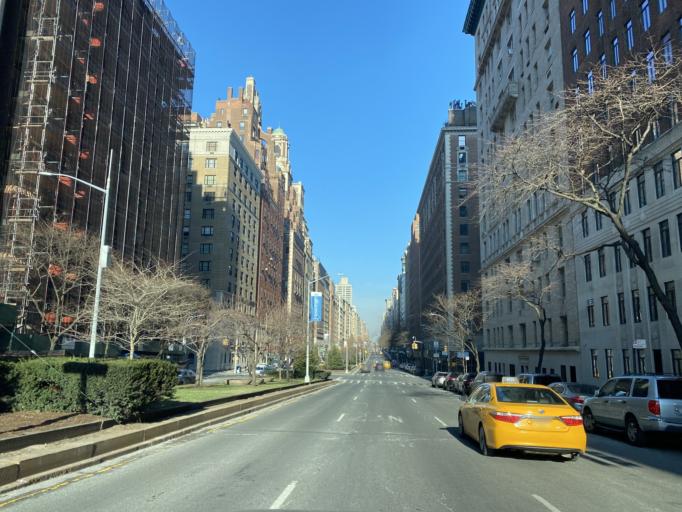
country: US
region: New York
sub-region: New York County
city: Manhattan
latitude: 40.7705
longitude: -73.9643
